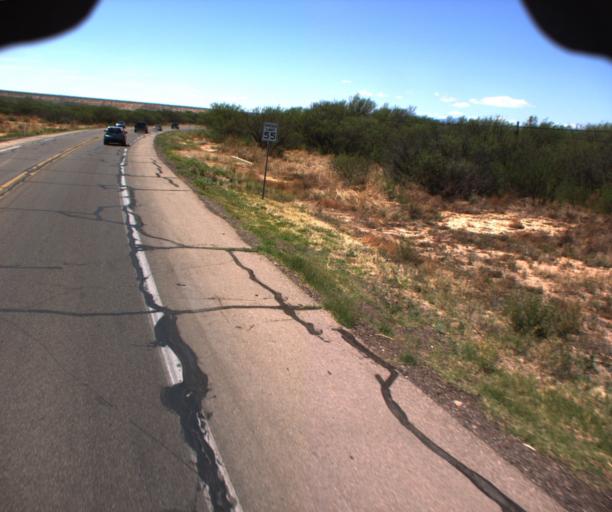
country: US
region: Arizona
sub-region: Cochise County
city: Saint David
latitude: 31.9055
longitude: -110.2509
